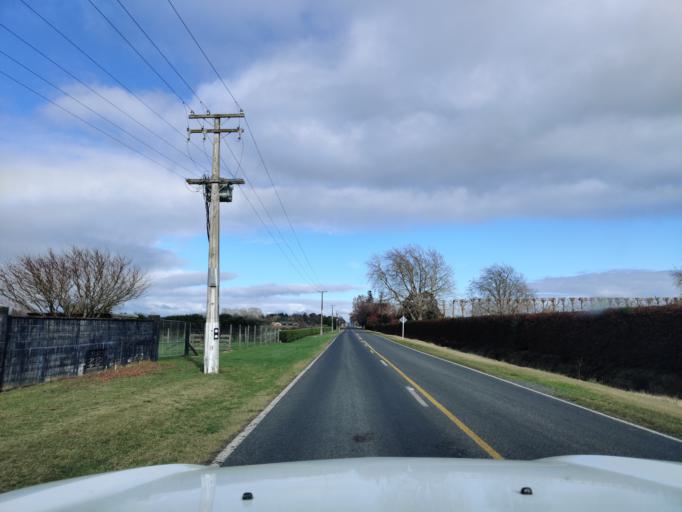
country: NZ
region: Waikato
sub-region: Waipa District
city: Cambridge
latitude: -37.8548
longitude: 175.4391
